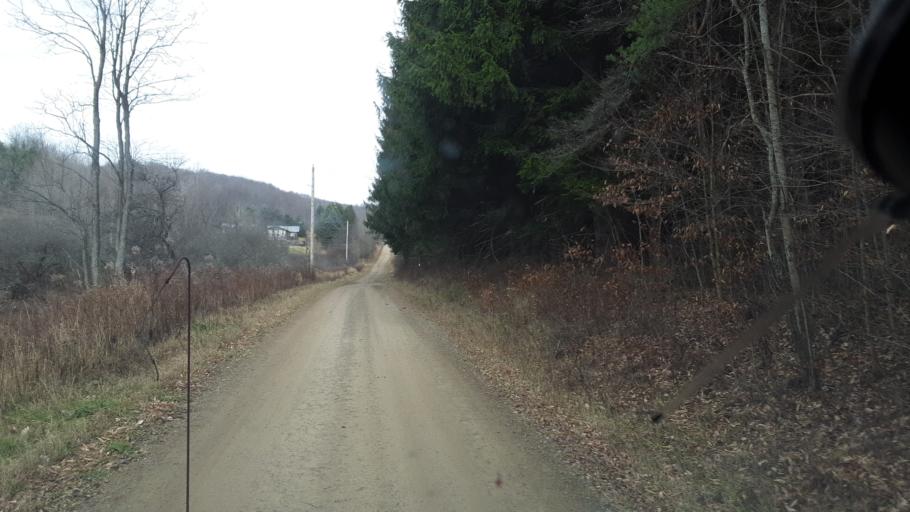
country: US
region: Pennsylvania
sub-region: Tioga County
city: Westfield
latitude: 41.9107
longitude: -77.7078
